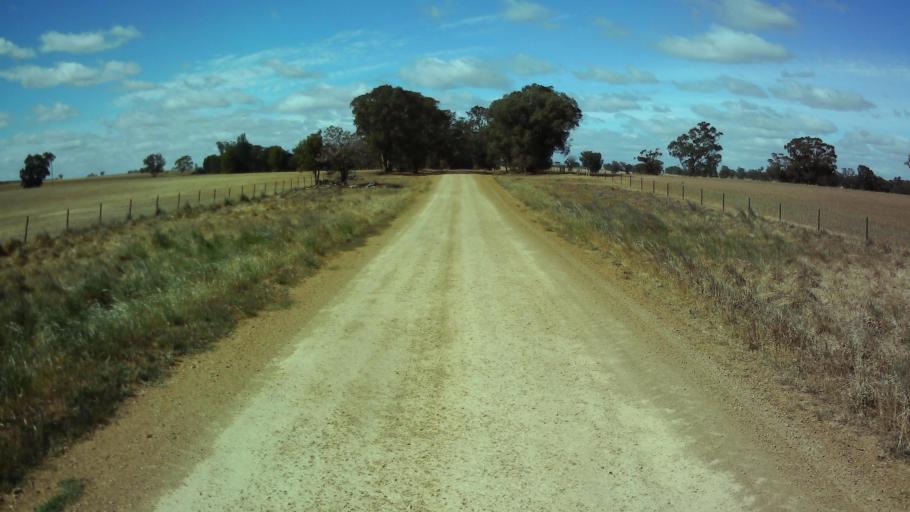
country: AU
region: New South Wales
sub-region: Weddin
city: Grenfell
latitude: -34.0621
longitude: 148.3118
